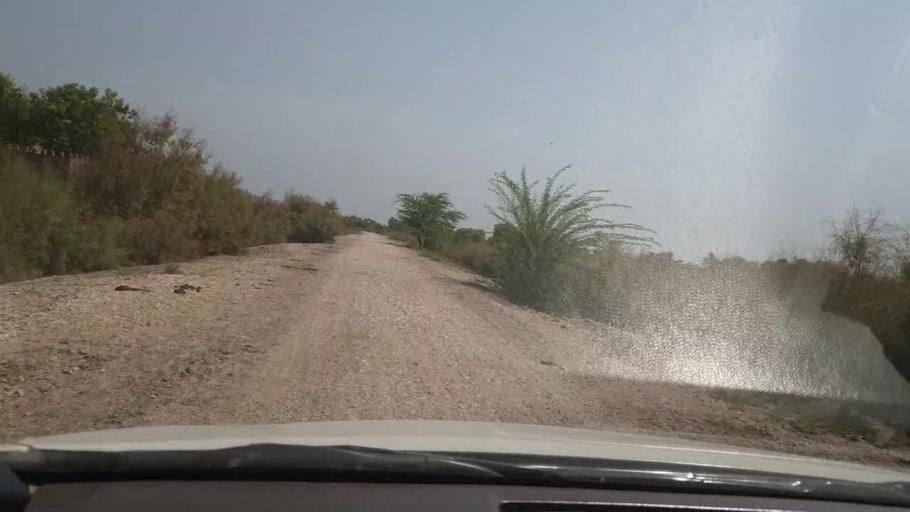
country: PK
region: Sindh
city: Shikarpur
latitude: 27.9285
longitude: 68.6045
